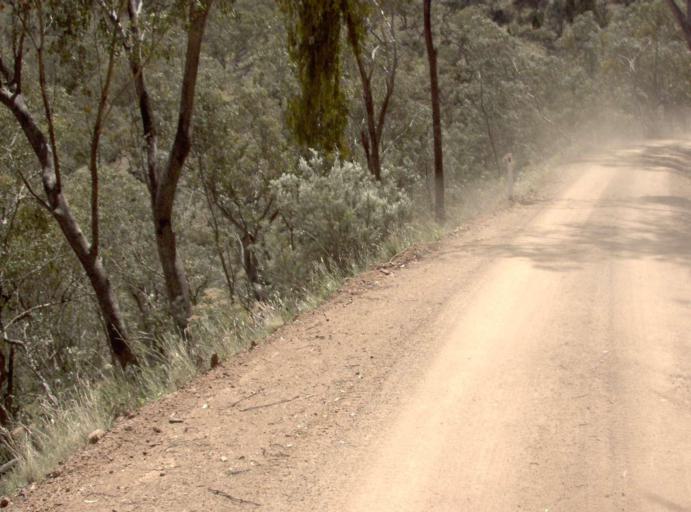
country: AU
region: New South Wales
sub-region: Snowy River
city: Jindabyne
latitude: -37.0843
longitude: 148.3963
